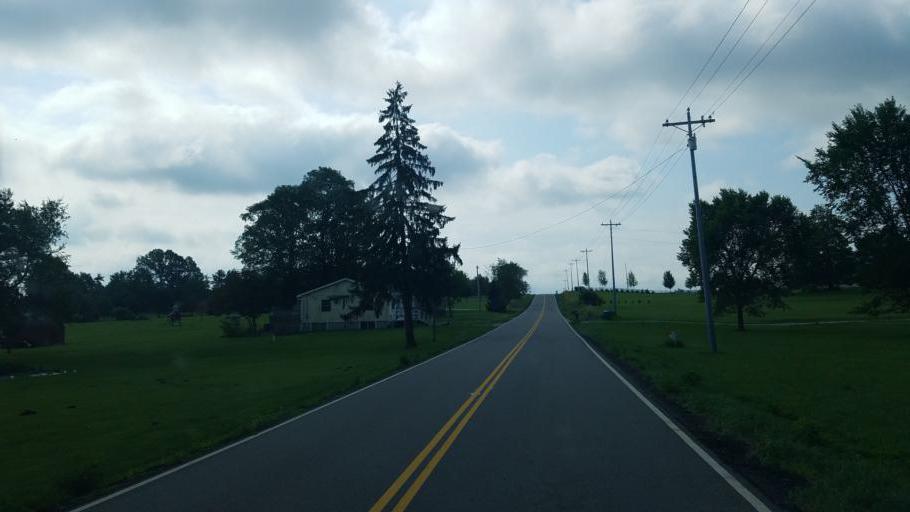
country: US
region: Ohio
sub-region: Licking County
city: Utica
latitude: 40.2437
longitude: -82.5802
